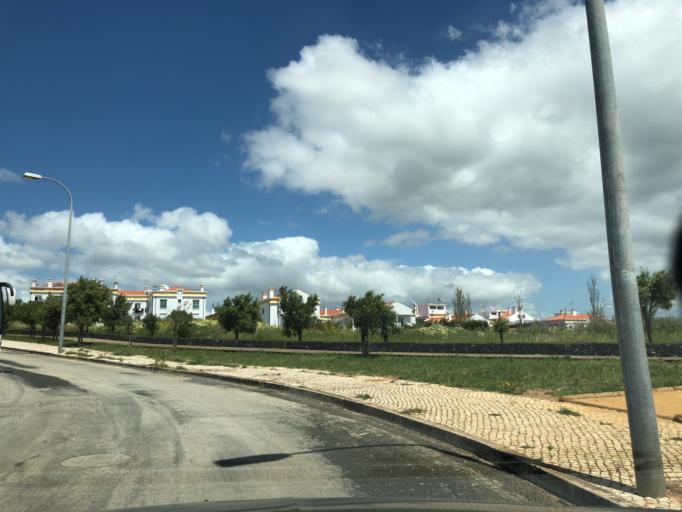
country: PT
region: Lisbon
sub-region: Cascais
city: Sao Domingos de Rana
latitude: 38.7137
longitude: -9.3257
